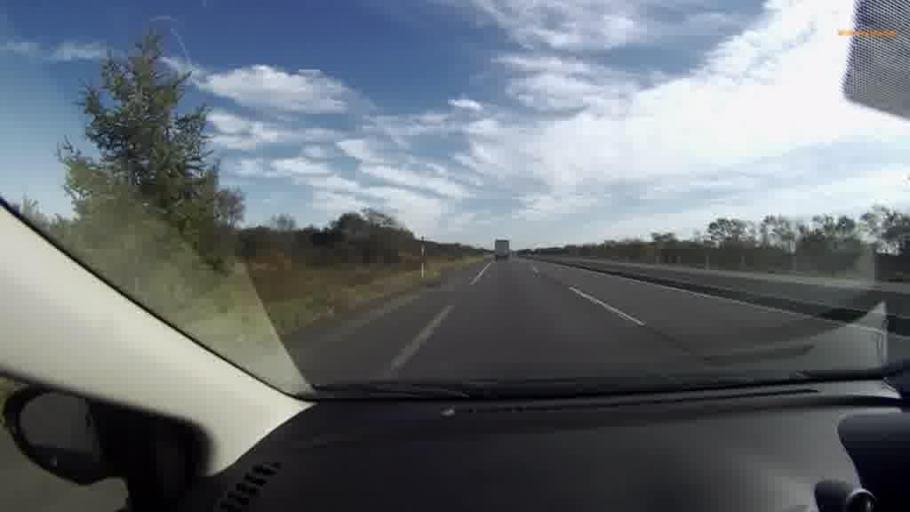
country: JP
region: Hokkaido
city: Kushiro
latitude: 43.0296
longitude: 144.2987
